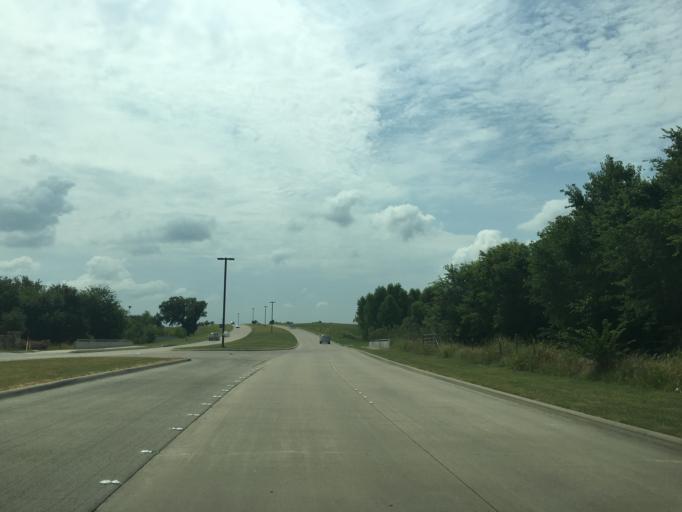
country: US
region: Texas
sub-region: Rockwall County
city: Rockwall
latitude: 32.9779
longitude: -96.4596
